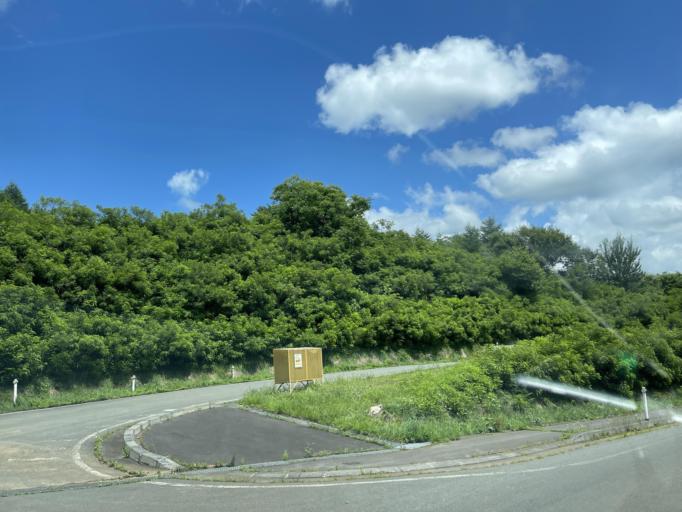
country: JP
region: Iwate
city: Ichinohe
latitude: 39.9734
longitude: 141.2134
